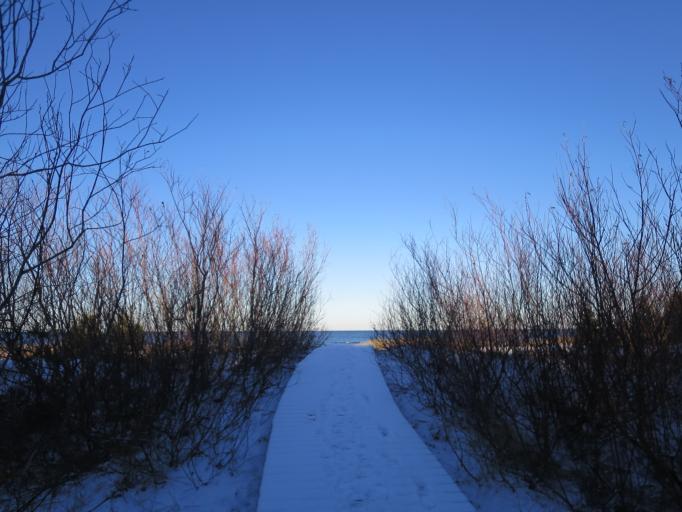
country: LV
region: Riga
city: Daugavgriva
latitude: 57.0708
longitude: 24.0643
